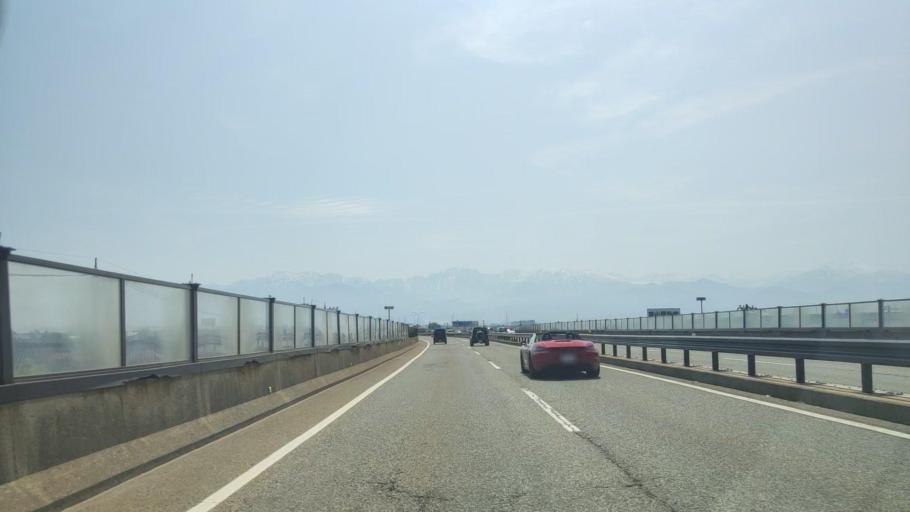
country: JP
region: Toyama
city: Toyama-shi
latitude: 36.7196
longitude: 137.2663
